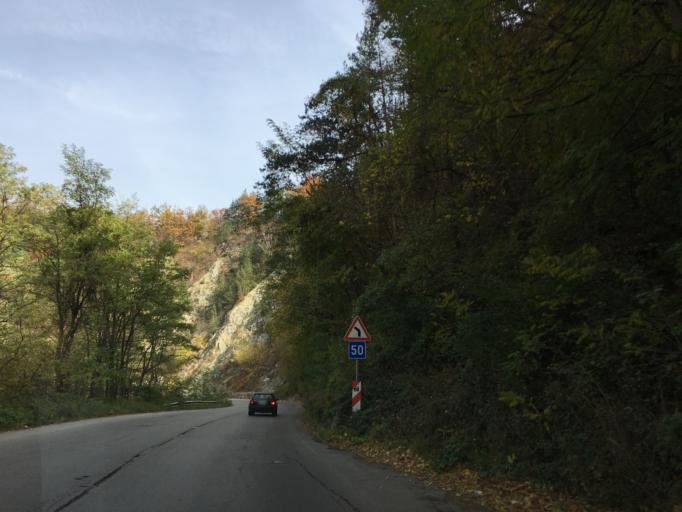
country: BG
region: Sofiya
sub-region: Obshtina Elin Pelin
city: Elin Pelin
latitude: 42.5566
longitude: 23.4500
